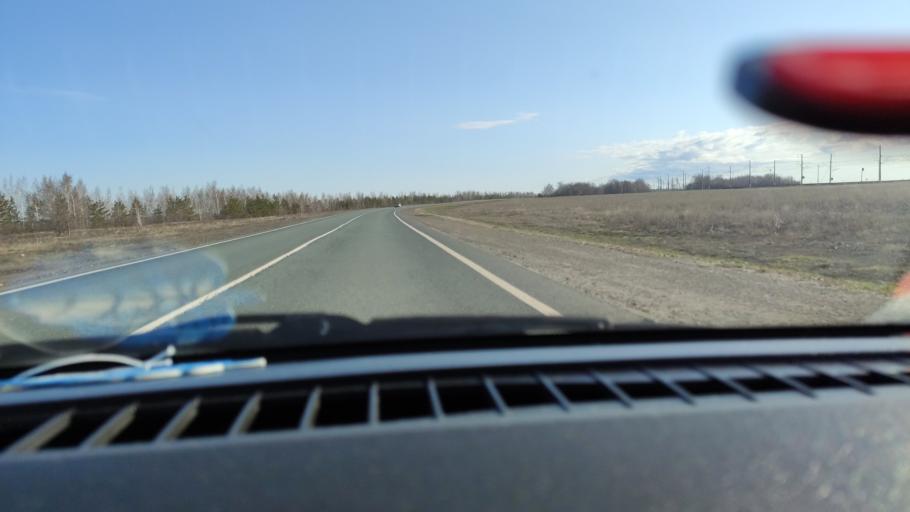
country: RU
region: Samara
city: Syzran'
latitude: 52.8611
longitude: 48.2652
